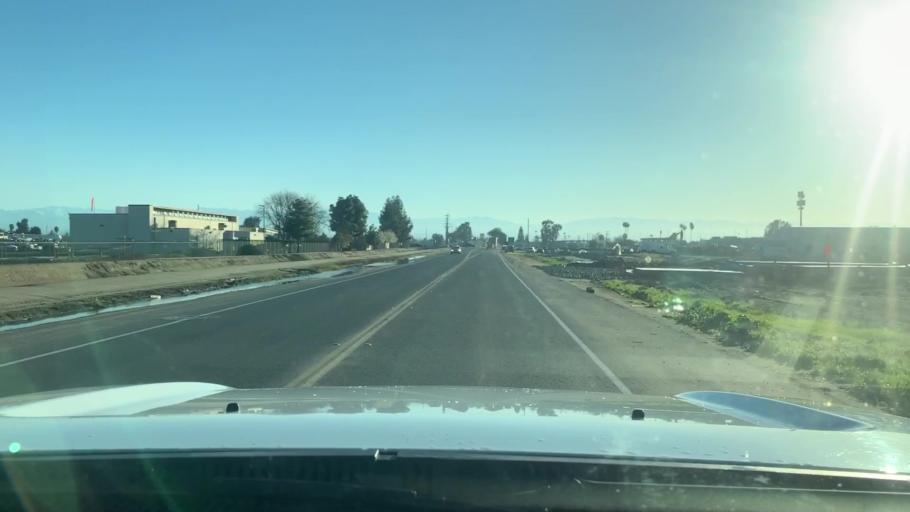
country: US
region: California
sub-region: Tulare County
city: Tulare
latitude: 36.1821
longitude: -119.3349
